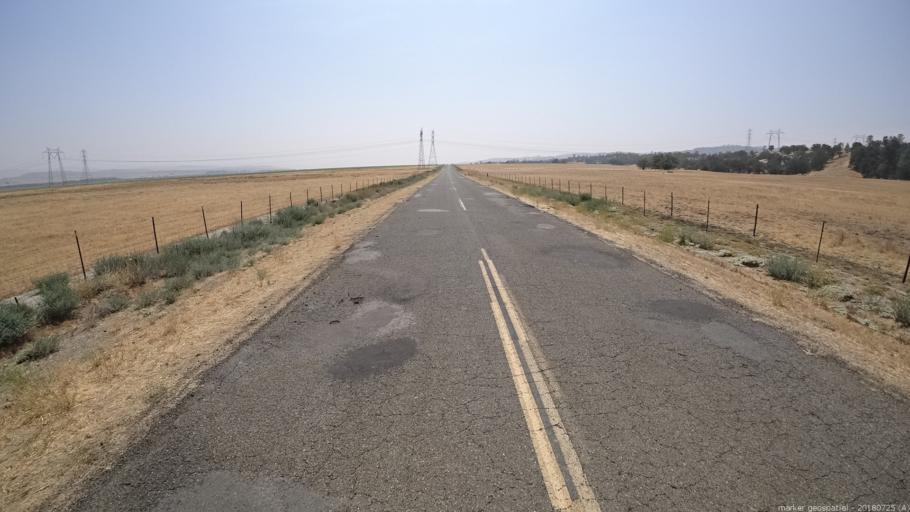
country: US
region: California
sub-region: San Luis Obispo County
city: Shandon
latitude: 35.8210
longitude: -120.3820
